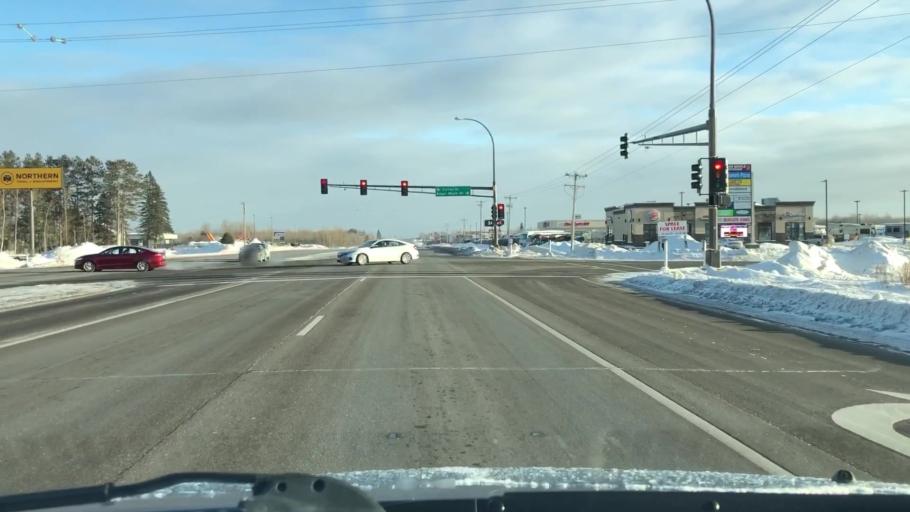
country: US
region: Minnesota
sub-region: Saint Louis County
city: Hermantown
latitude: 46.8338
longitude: -92.2059
